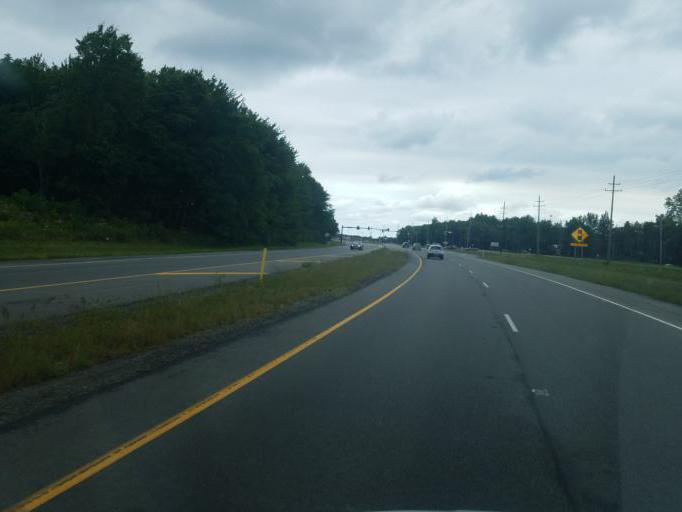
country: US
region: Ohio
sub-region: Lake County
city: Painesville
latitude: 41.6561
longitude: -81.2401
